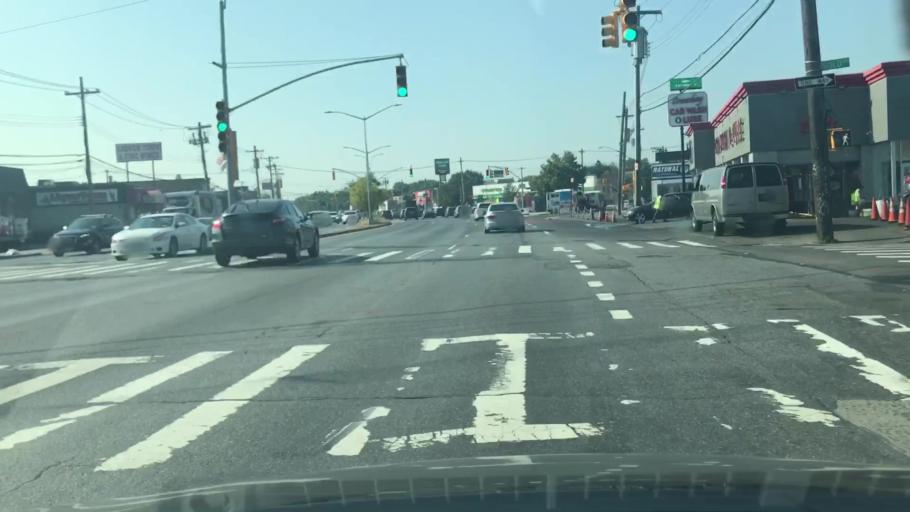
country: US
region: New York
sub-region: Queens County
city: Borough of Queens
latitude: 40.6738
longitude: -73.8434
